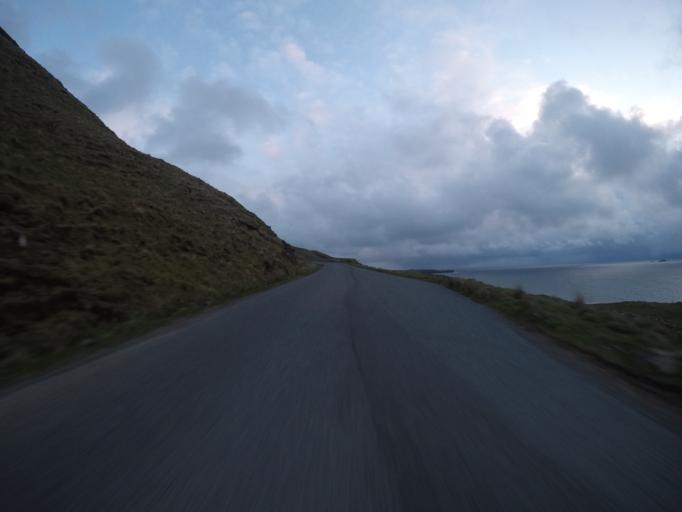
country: GB
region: Scotland
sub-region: Highland
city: Portree
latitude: 57.6660
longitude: -6.3585
